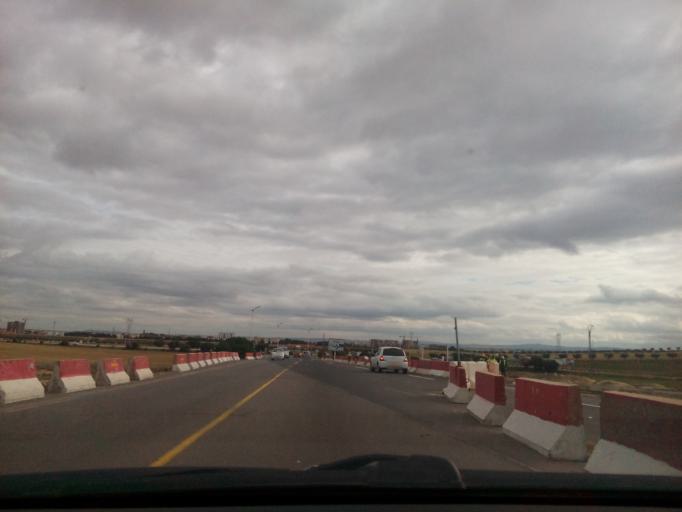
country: DZ
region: Sidi Bel Abbes
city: Sidi Bel Abbes
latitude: 35.2161
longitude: -0.6689
